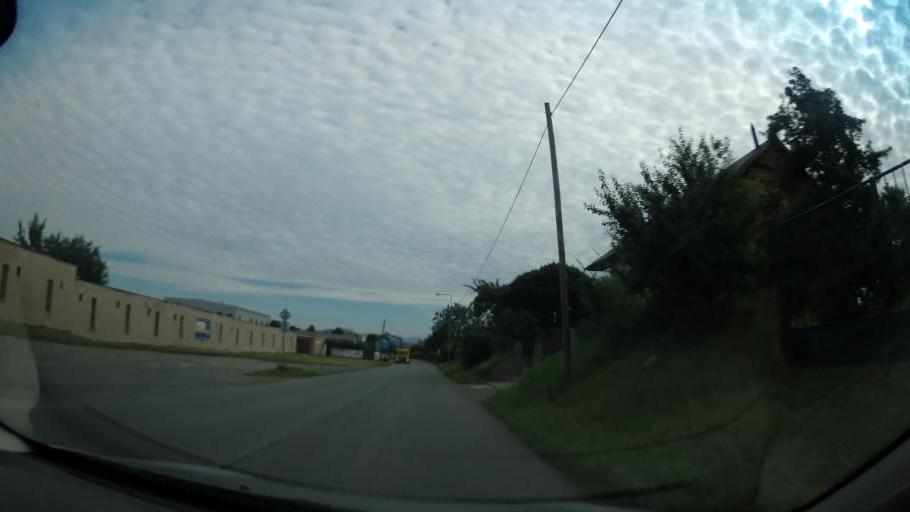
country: CZ
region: Olomoucky
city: Zabreh
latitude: 49.8868
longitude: 16.8767
